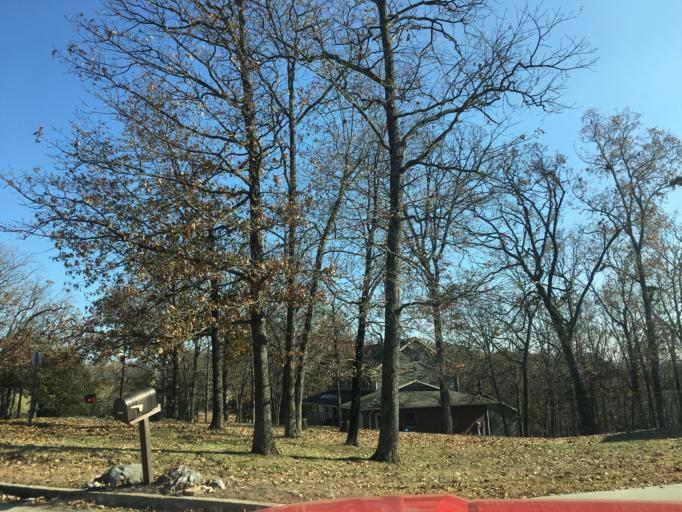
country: US
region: Missouri
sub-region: Cole County
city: Wardsville
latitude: 38.4840
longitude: -92.1817
